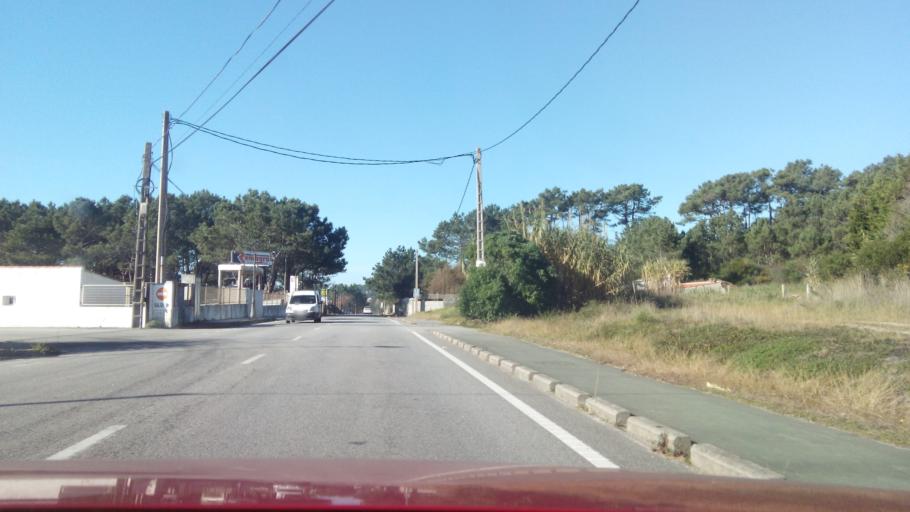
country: ES
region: Galicia
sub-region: Provincia de Pontevedra
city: O Grove
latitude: 42.4590
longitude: -8.8906
